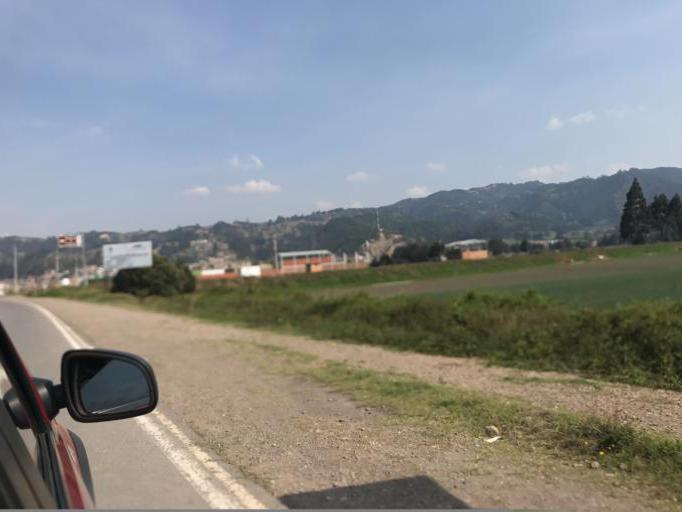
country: CO
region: Boyaca
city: Samaca
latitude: 5.4993
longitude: -73.4911
